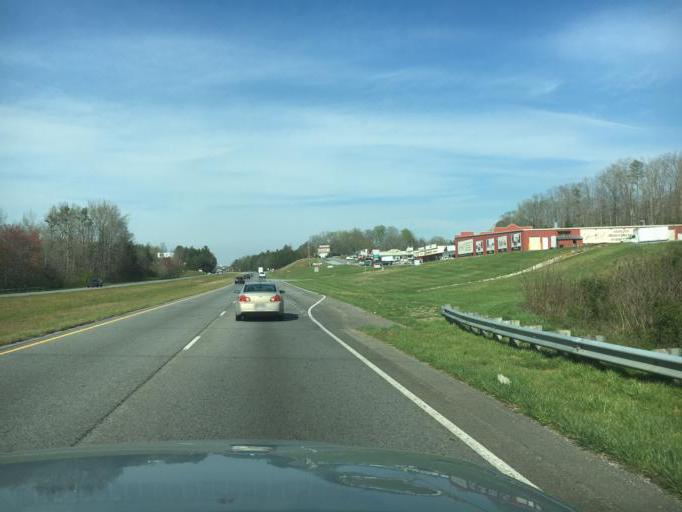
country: US
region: Georgia
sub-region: Banks County
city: Alto
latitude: 34.4729
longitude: -83.5943
